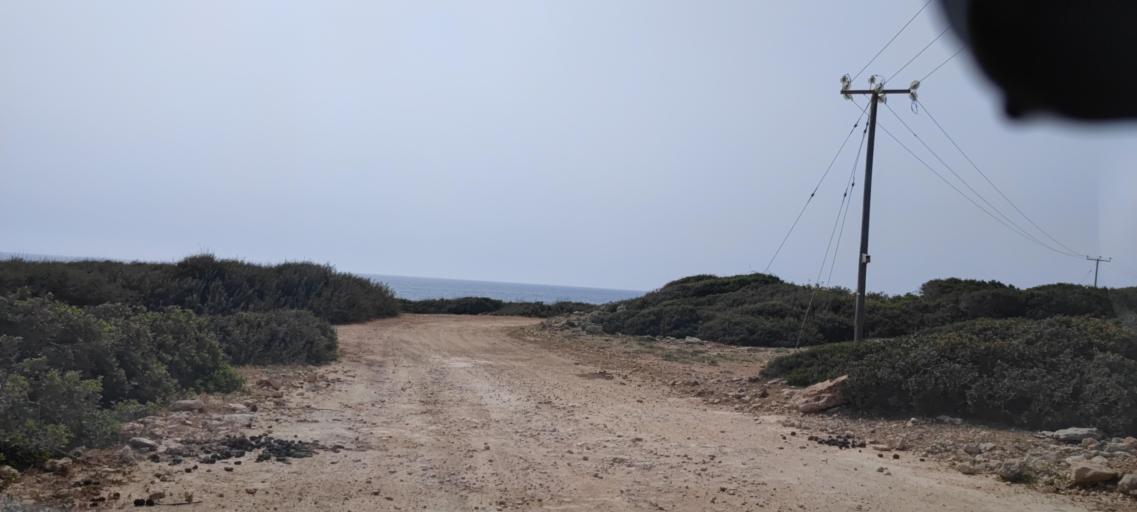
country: CY
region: Ammochostos
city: Rizokarpaso
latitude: 35.6784
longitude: 34.5775
